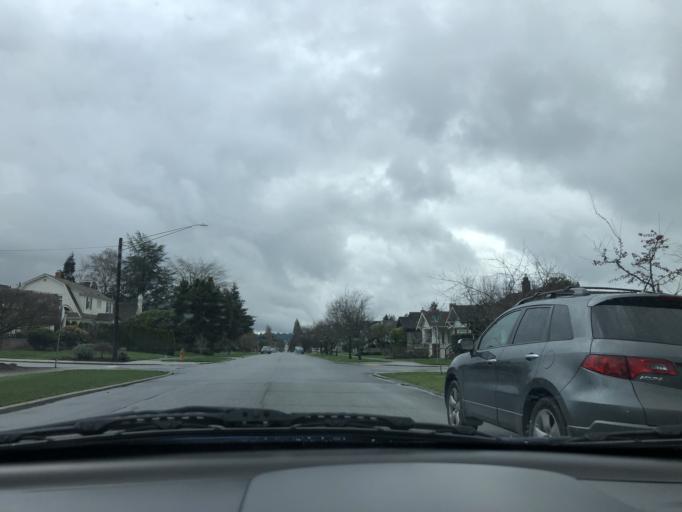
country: US
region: Washington
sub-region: Snohomish County
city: Everett
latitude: 48.0034
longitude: -122.2108
